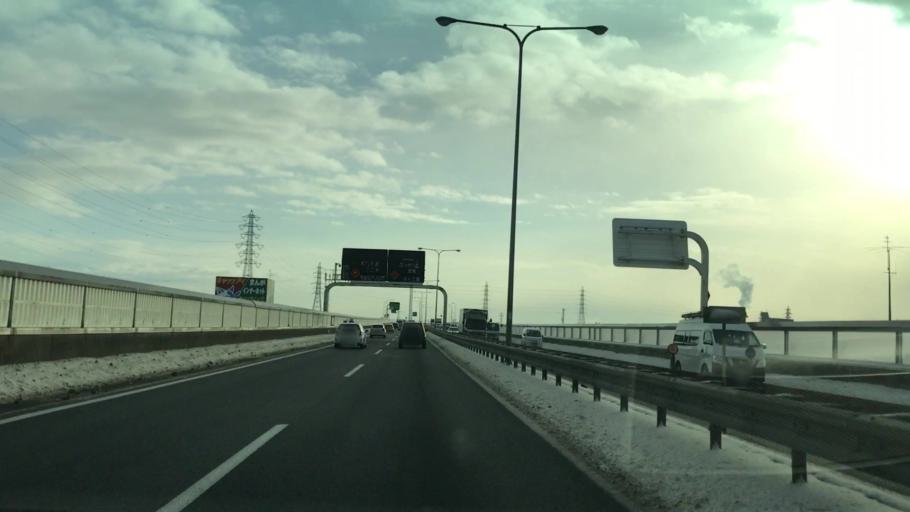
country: JP
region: Hokkaido
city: Sapporo
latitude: 43.0927
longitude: 141.4051
